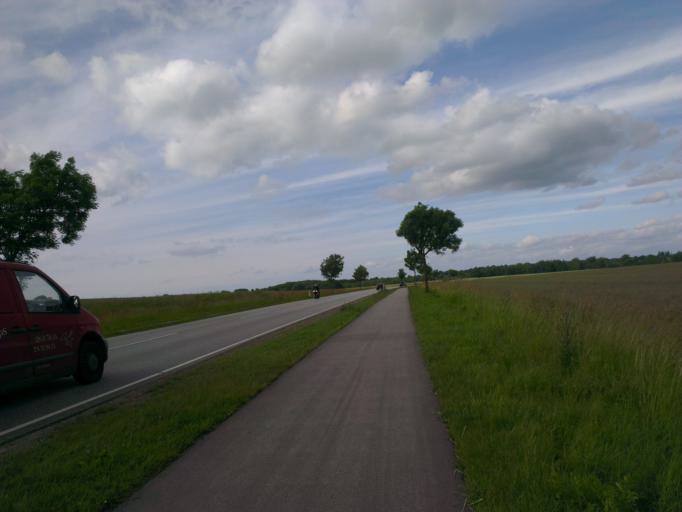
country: DK
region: Capital Region
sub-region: Frederikssund Kommune
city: Skibby
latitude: 55.7307
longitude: 11.9459
